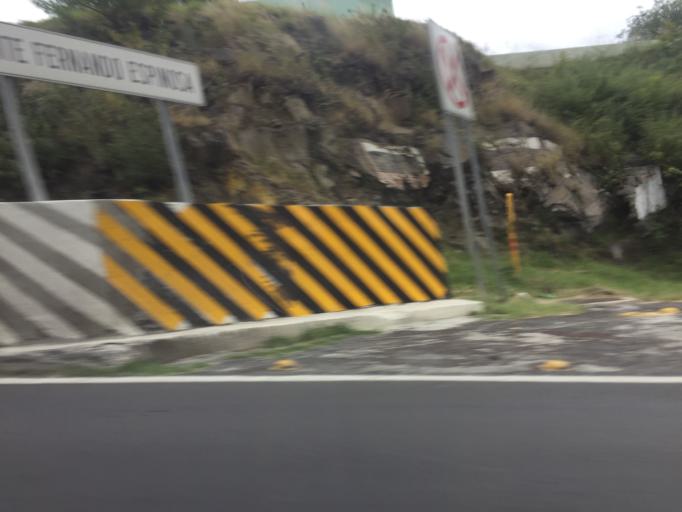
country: MX
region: Jalisco
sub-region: Tonala
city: Mismaloya (Fraccionamiento Pedregal de Santa Martha)
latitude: 20.6019
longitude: -103.1477
